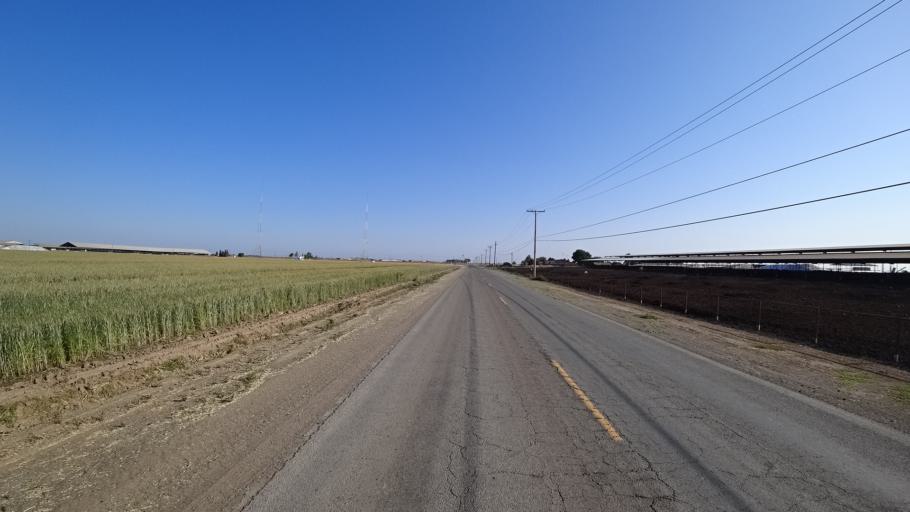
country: US
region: California
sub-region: Kings County
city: Home Garden
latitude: 36.3225
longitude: -119.5652
